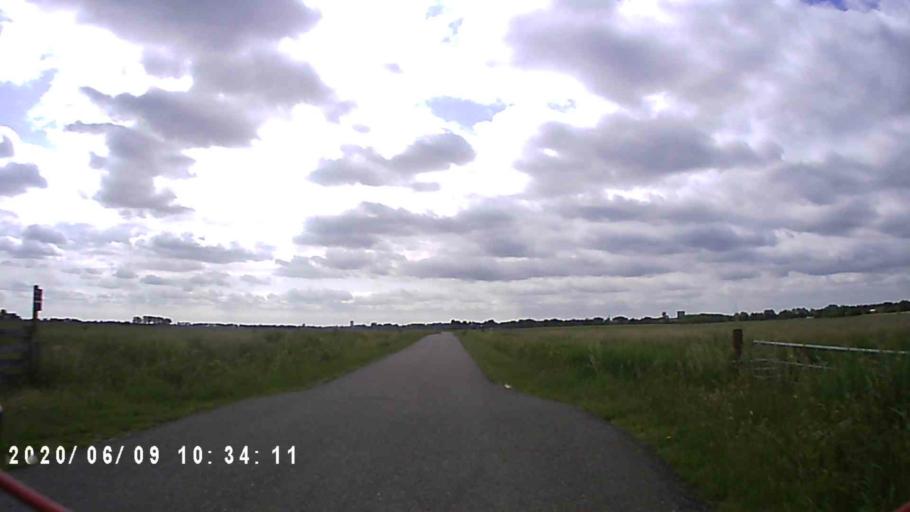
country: NL
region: Groningen
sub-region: Gemeente Zuidhorn
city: Aduard
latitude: 53.2650
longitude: 6.5161
